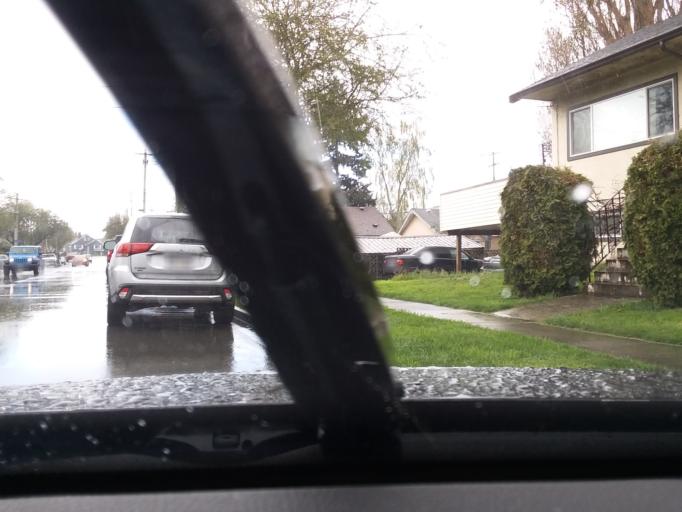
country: CA
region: British Columbia
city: Victoria
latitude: 48.4363
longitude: -123.3500
